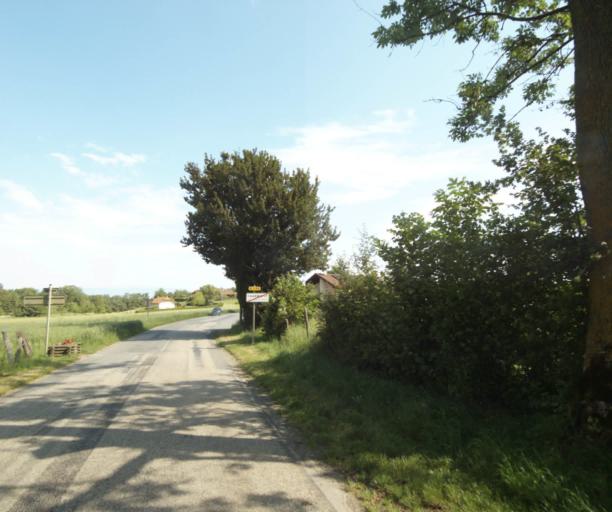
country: FR
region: Rhone-Alpes
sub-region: Departement de la Haute-Savoie
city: Lyaud
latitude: 46.3217
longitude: 6.4993
